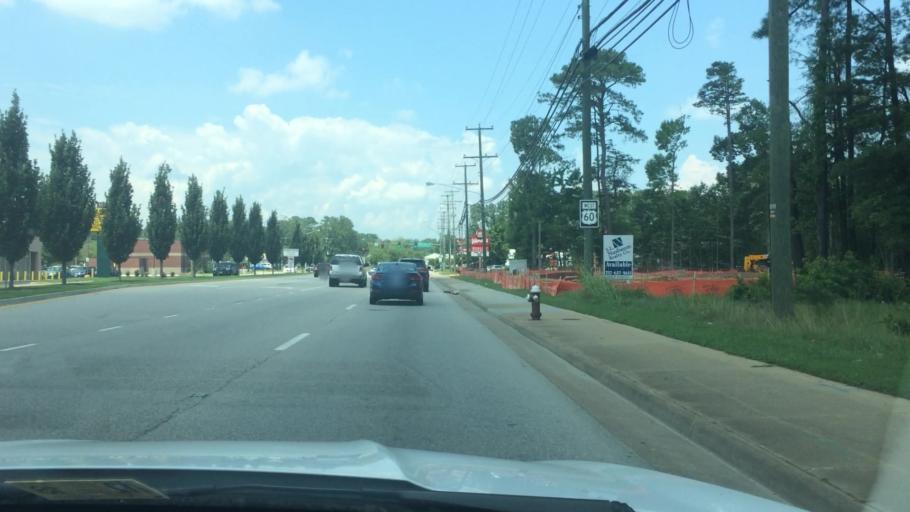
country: US
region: Virginia
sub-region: York County
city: Yorktown
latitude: 37.1569
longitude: -76.5561
